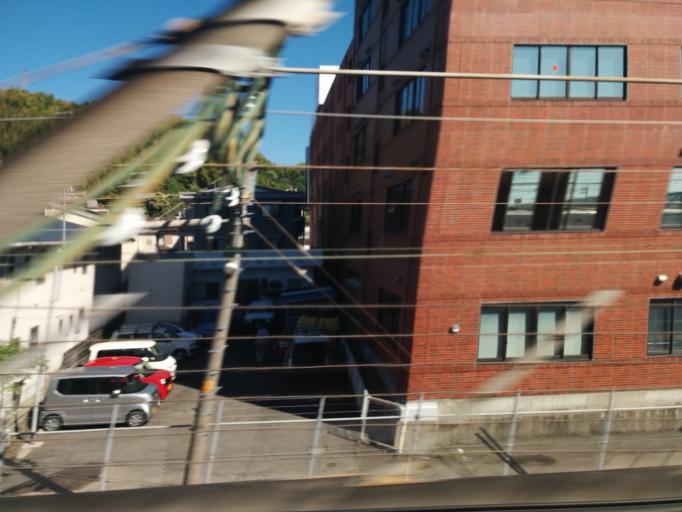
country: JP
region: Shizuoka
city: Shizuoka-shi
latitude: 34.9805
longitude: 138.4065
